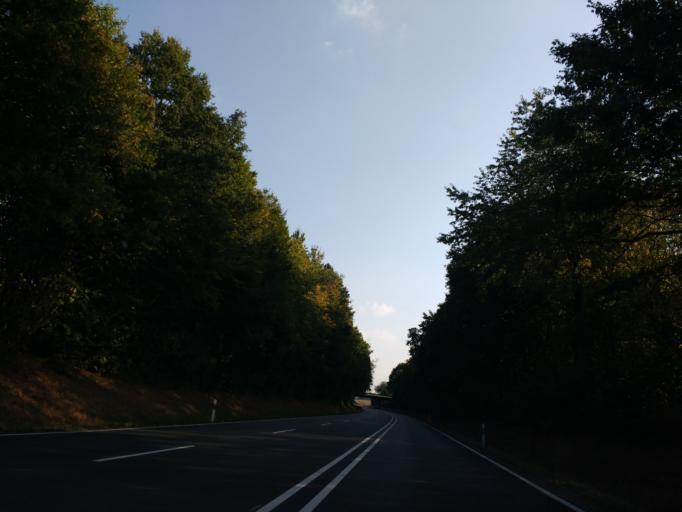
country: DE
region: North Rhine-Westphalia
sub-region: Regierungsbezirk Detmold
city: Steinheim
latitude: 51.8887
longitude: 9.0900
